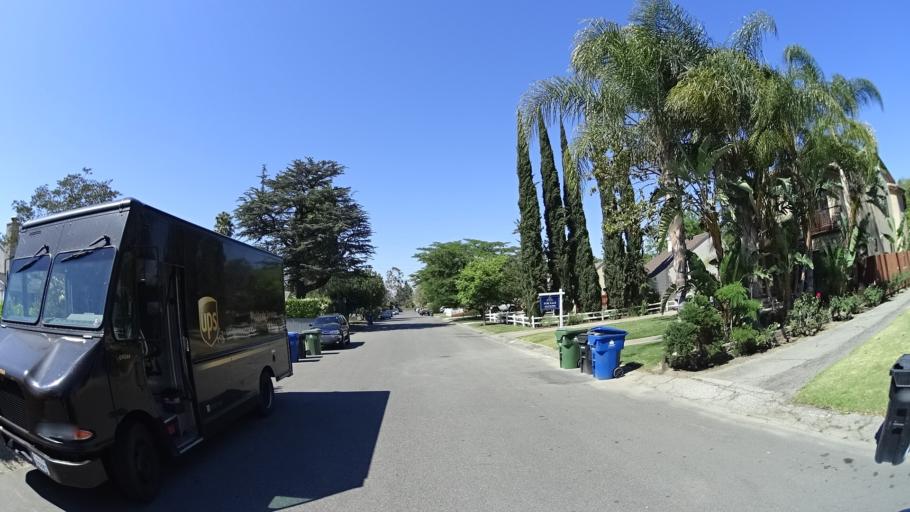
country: US
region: California
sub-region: Los Angeles County
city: North Hollywood
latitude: 34.1707
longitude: -118.3909
